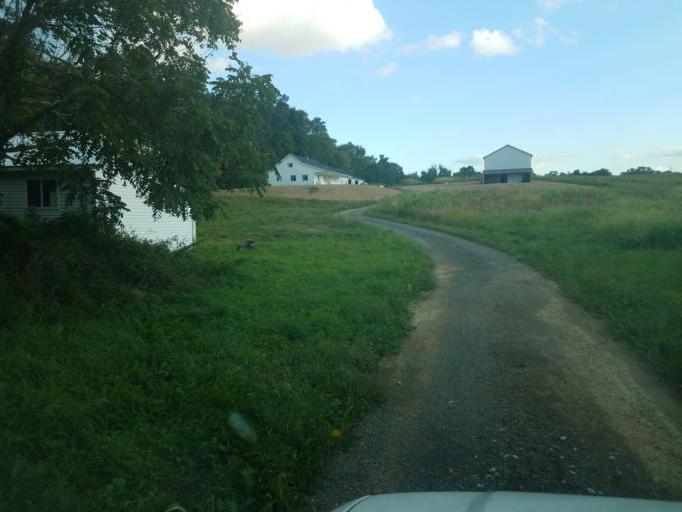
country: US
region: Ohio
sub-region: Knox County
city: Fredericktown
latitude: 40.5116
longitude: -82.6643
